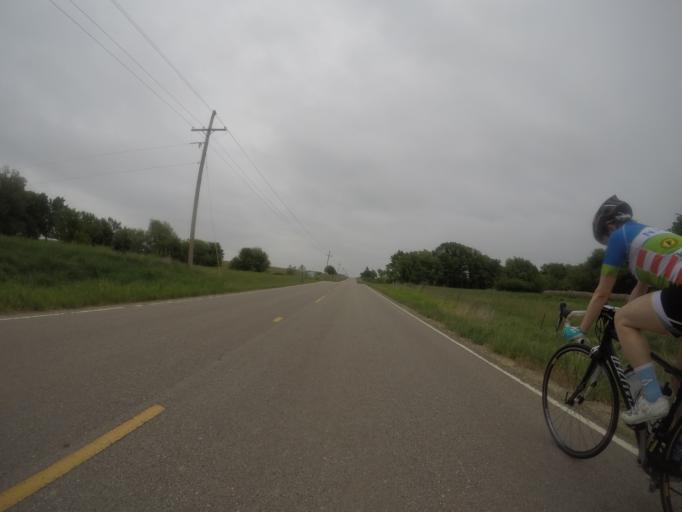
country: US
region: Kansas
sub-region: Pottawatomie County
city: Westmoreland
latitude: 39.5222
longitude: -96.2635
